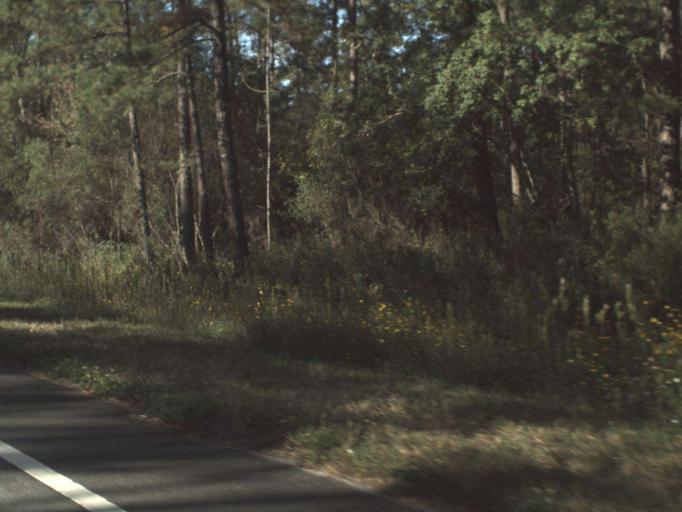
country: US
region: Florida
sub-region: Gadsden County
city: Midway
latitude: 30.3769
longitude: -84.5582
